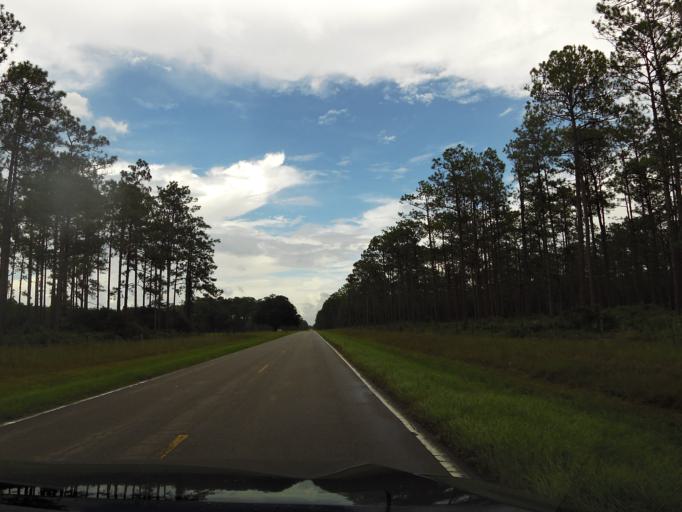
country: US
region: Florida
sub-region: Duval County
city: Baldwin
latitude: 30.3996
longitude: -81.9953
